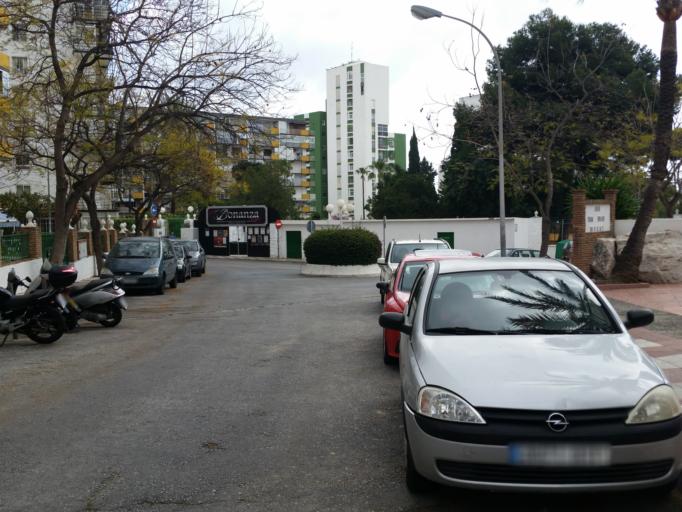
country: ES
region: Andalusia
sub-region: Provincia de Malaga
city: Torremolinos
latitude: 36.5967
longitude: -4.5255
